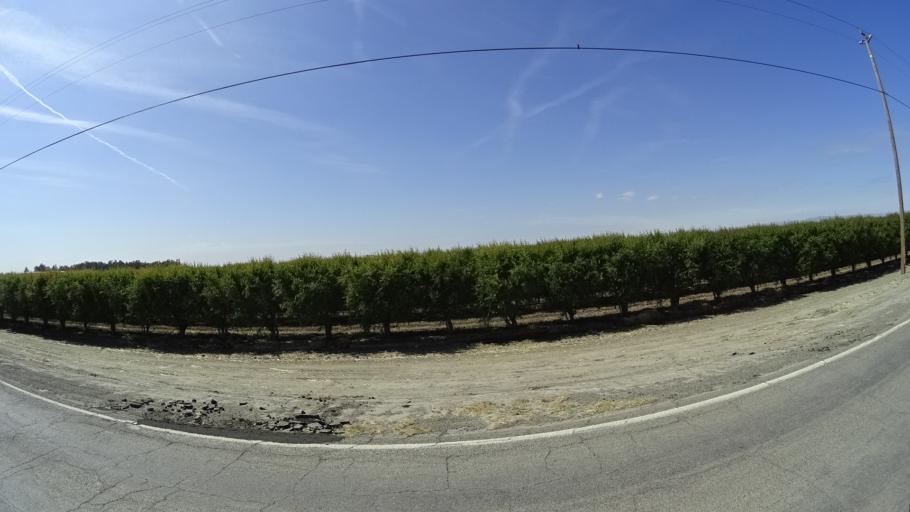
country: US
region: California
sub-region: Kings County
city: Lemoore
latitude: 36.2551
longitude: -119.8221
